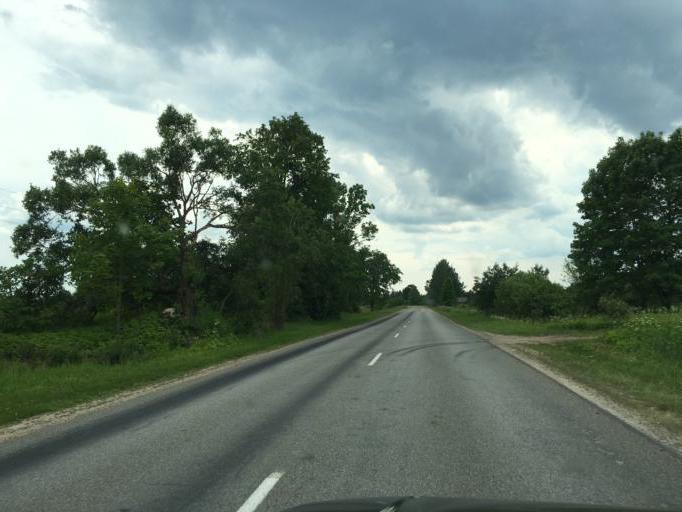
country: LV
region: Rugaju
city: Rugaji
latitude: 56.9129
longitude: 27.0674
